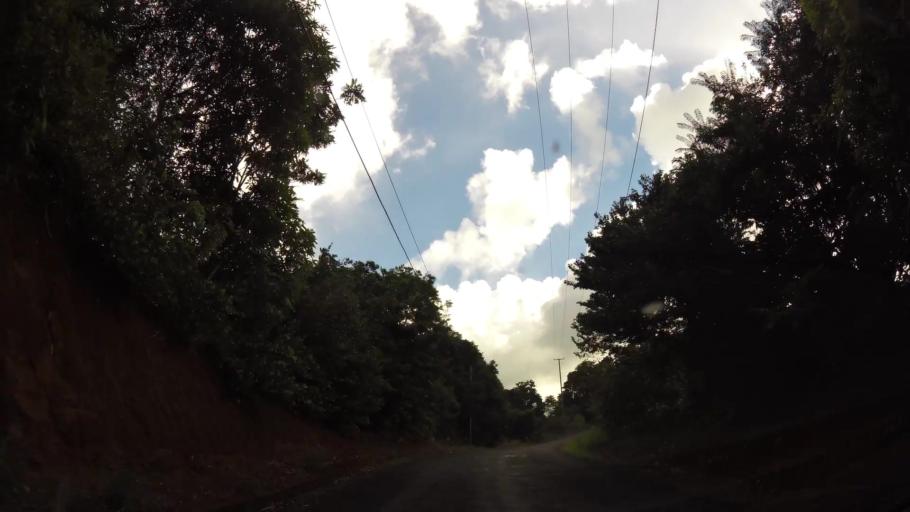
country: DM
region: Saint Andrew
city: Calibishie
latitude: 15.5957
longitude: -61.3945
